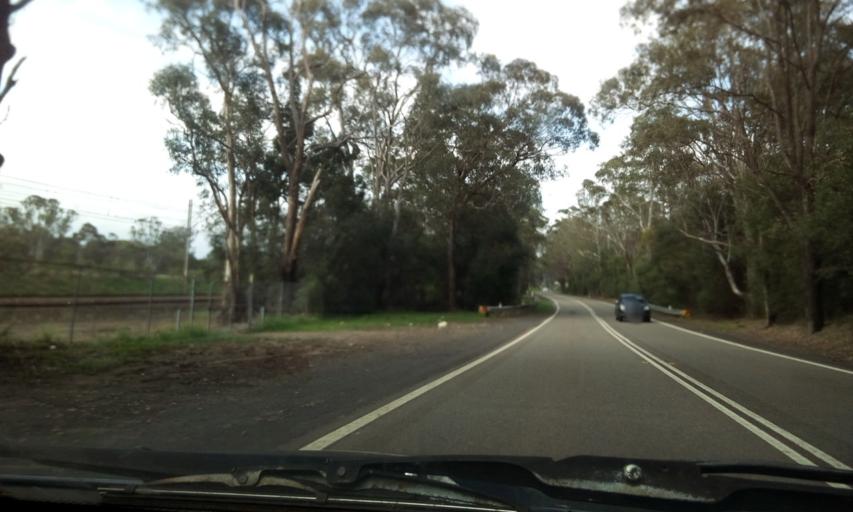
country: AU
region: New South Wales
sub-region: Campbelltown Municipality
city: Glen Alpine
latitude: -34.0805
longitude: 150.7805
